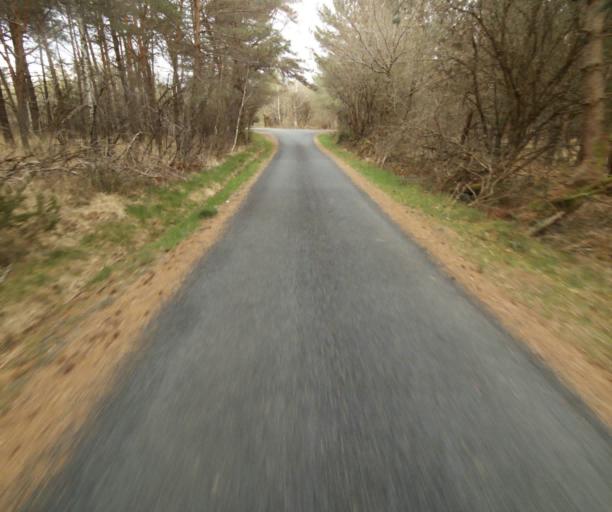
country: FR
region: Limousin
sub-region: Departement de la Correze
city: Saint-Privat
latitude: 45.1992
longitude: 2.0039
